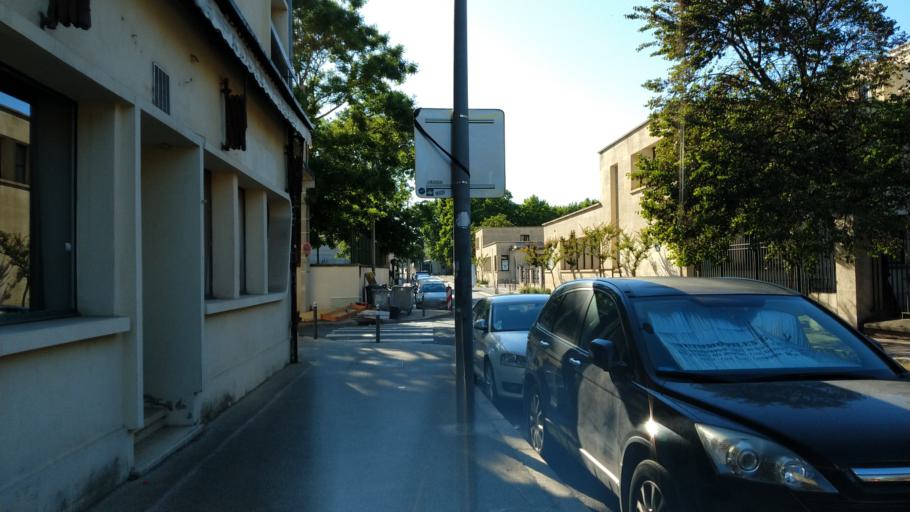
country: FR
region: Languedoc-Roussillon
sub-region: Departement de l'Herault
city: Montpellier
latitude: 43.6161
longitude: 3.8713
